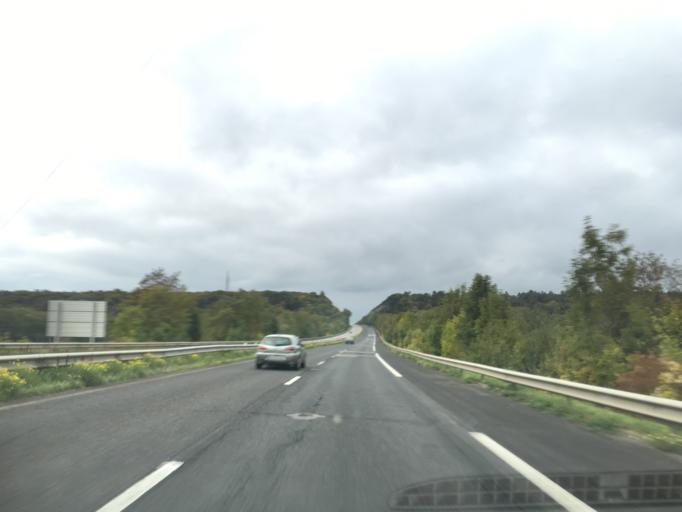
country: FR
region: Lorraine
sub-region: Departement de Meurthe-et-Moselle
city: Foug
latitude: 48.6710
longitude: 5.7804
